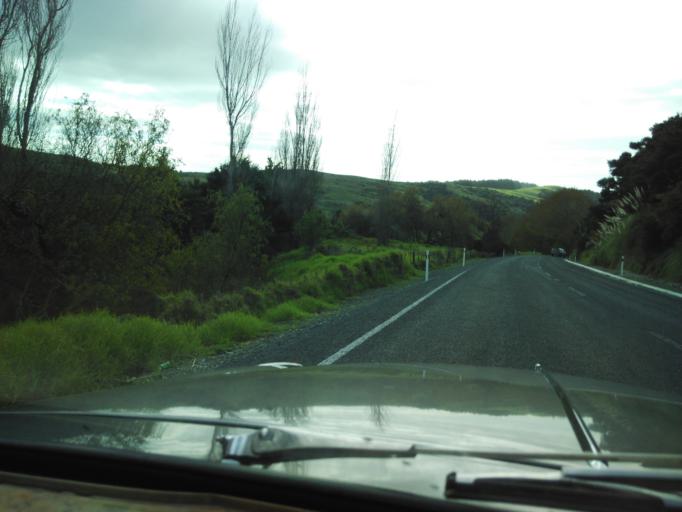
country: NZ
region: Auckland
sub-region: Auckland
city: Wellsford
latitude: -36.3457
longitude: 174.3658
